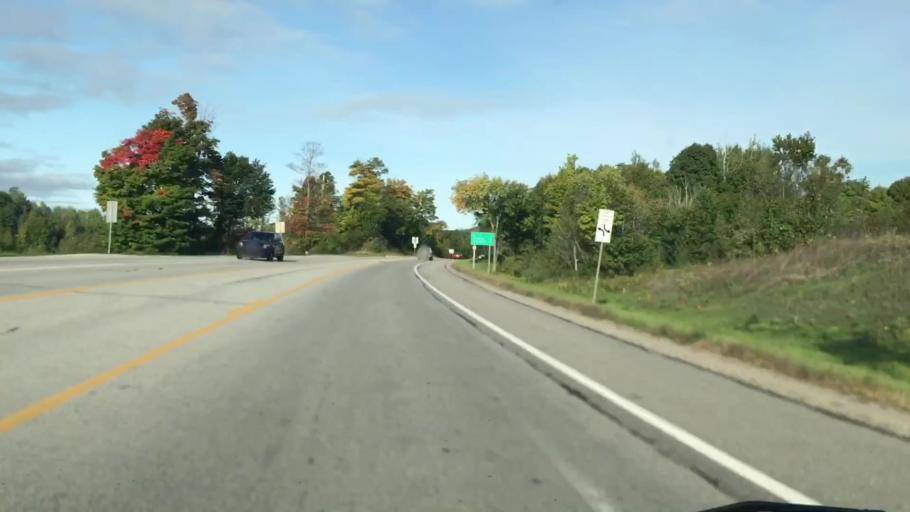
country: US
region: Michigan
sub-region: Luce County
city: Newberry
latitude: 46.3037
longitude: -85.5125
